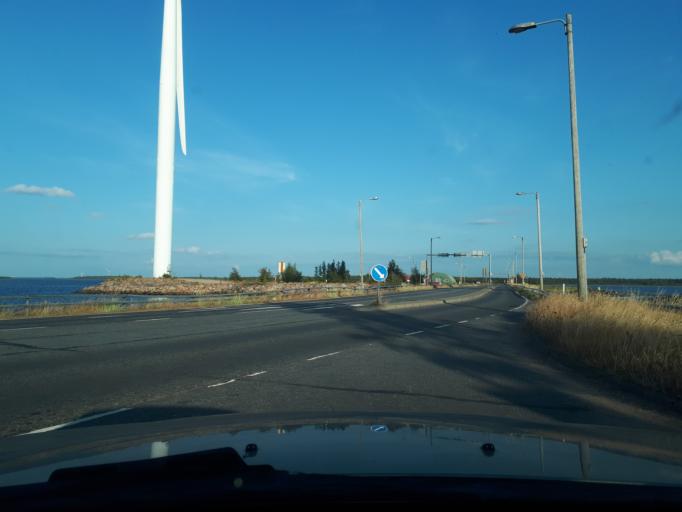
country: FI
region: Northern Ostrobothnia
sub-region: Oulu
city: Lumijoki
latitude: 65.0084
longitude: 25.1974
